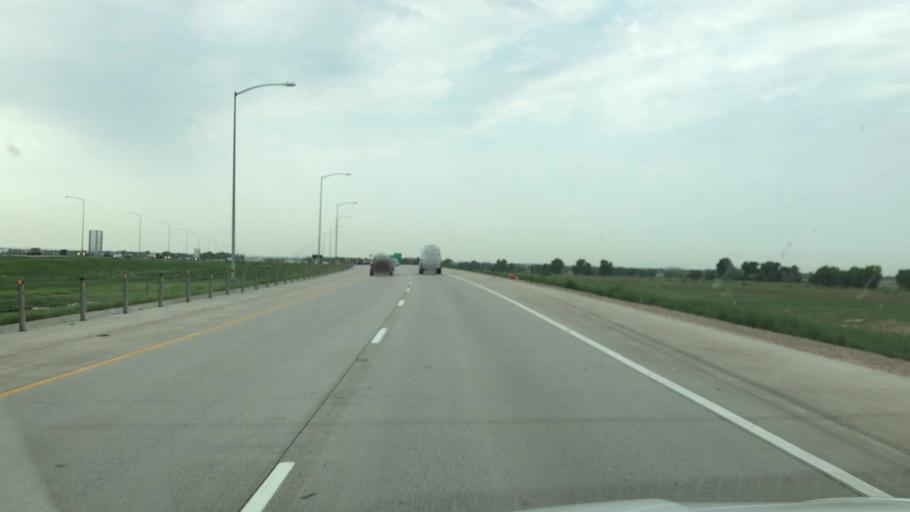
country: US
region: Colorado
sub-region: Adams County
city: Aurora
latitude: 39.8213
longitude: -104.7869
